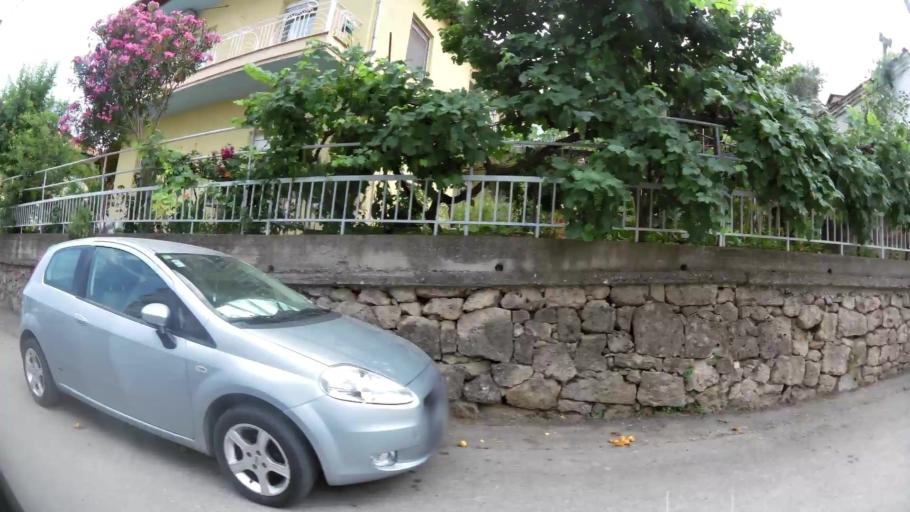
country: GR
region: Central Macedonia
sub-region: Nomos Imathias
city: Veroia
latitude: 40.5123
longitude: 22.2139
